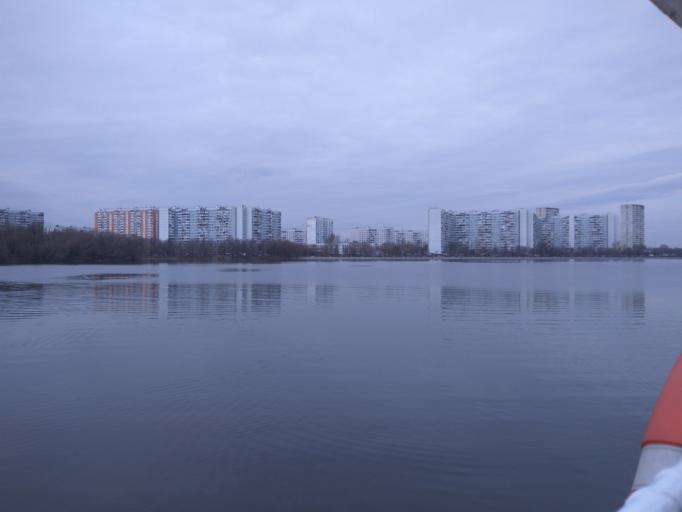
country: RU
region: Moscow
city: Mar'ino
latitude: 55.6777
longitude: 37.7136
